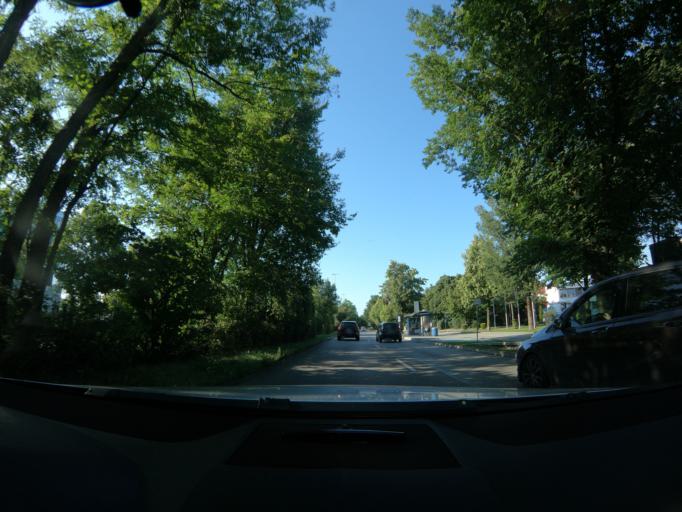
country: DE
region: Bavaria
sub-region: Upper Bavaria
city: Bogenhausen
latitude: 48.1923
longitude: 11.5841
